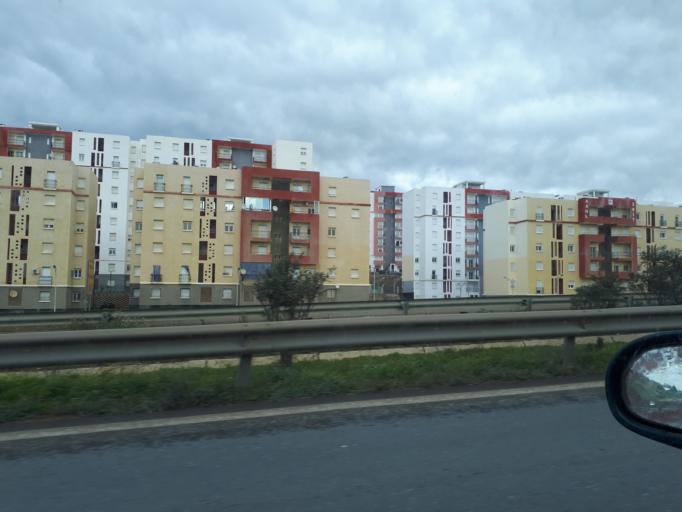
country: DZ
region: Tipaza
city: Douera
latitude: 36.7084
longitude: 2.9297
